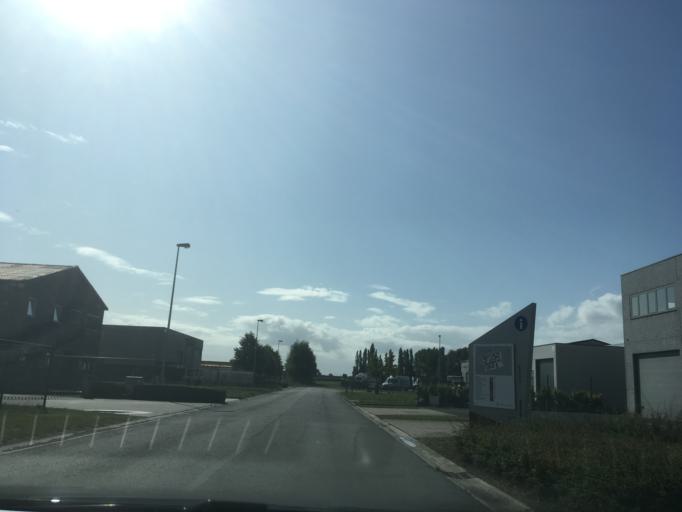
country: BE
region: Flanders
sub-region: Provincie West-Vlaanderen
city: Kortemark
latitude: 51.0229
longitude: 3.0481
